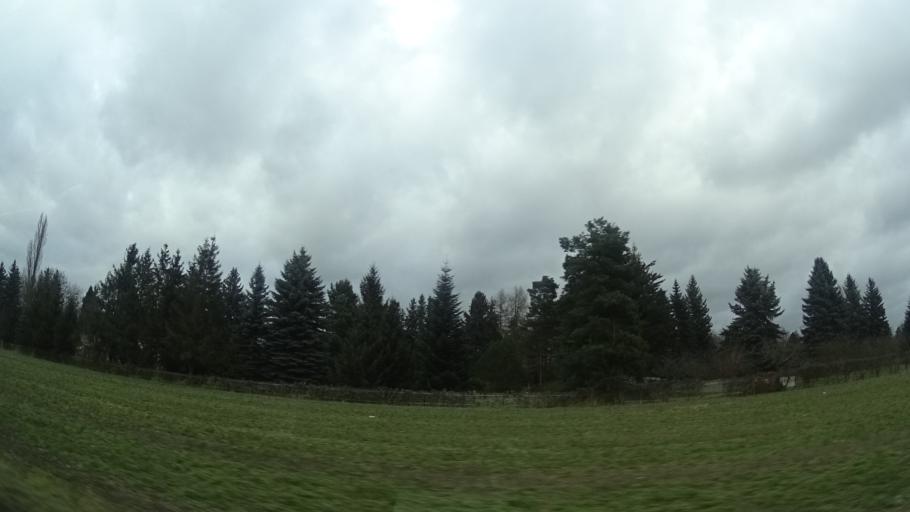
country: DE
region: Thuringia
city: Zeulenroda
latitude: 50.6326
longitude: 11.9917
